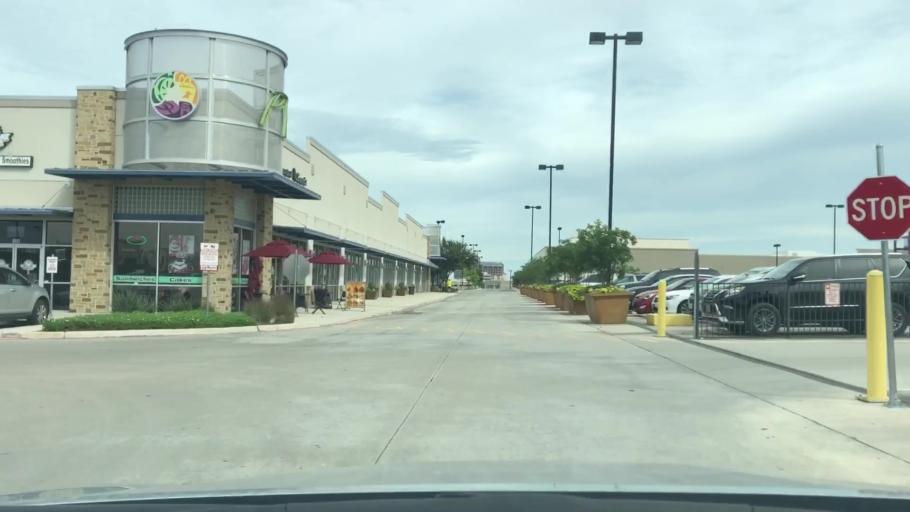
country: US
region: Texas
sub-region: Bexar County
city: Castle Hills
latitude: 29.5189
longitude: -98.5036
